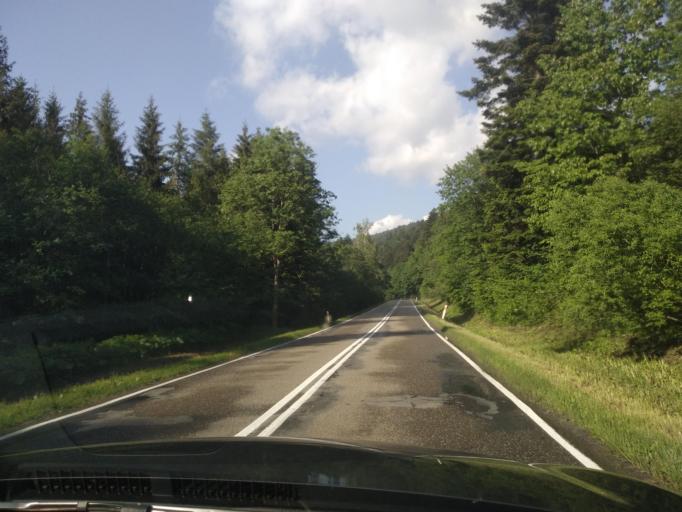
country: PL
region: Subcarpathian Voivodeship
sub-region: Powiat leski
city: Baligrod
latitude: 49.2993
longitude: 22.2728
